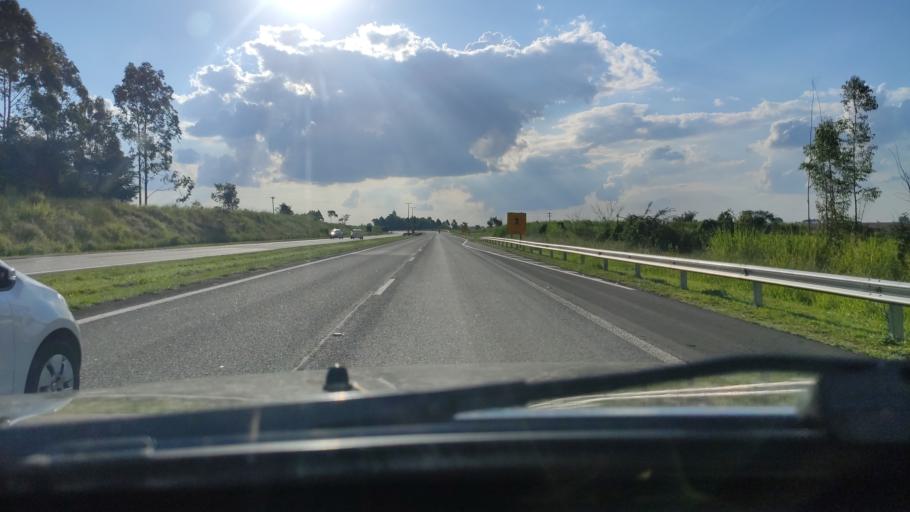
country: BR
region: Sao Paulo
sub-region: Itapira
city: Itapira
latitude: -22.4498
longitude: -46.8790
